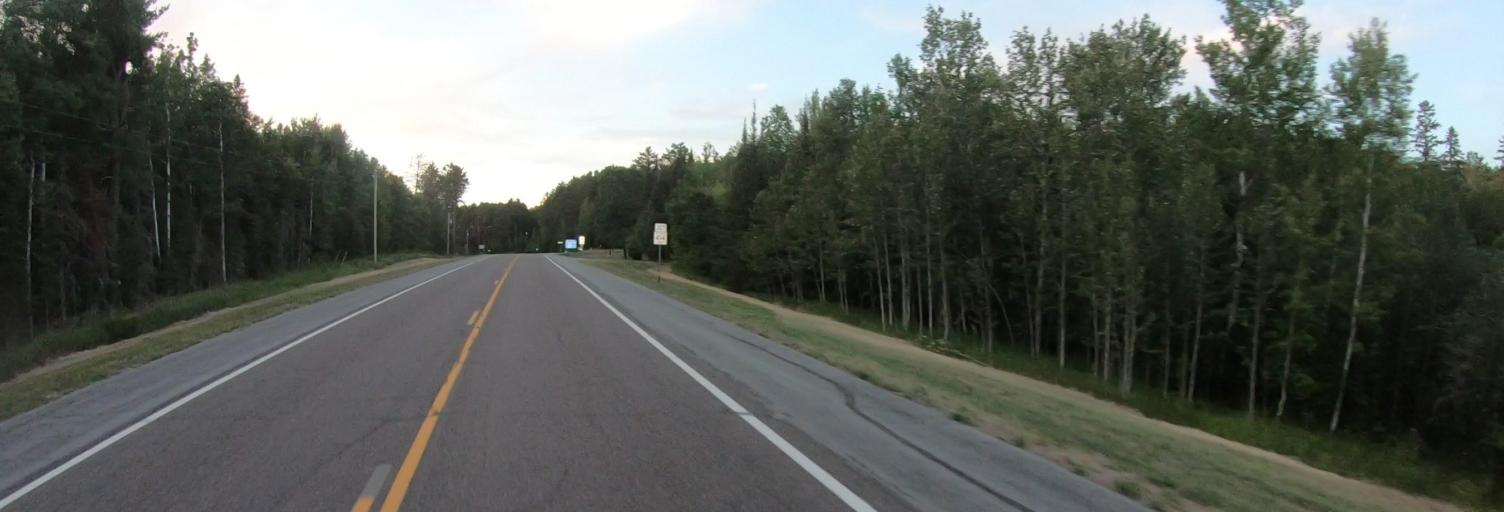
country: US
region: Minnesota
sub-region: Saint Louis County
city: Aurora
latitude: 47.8374
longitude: -92.3724
